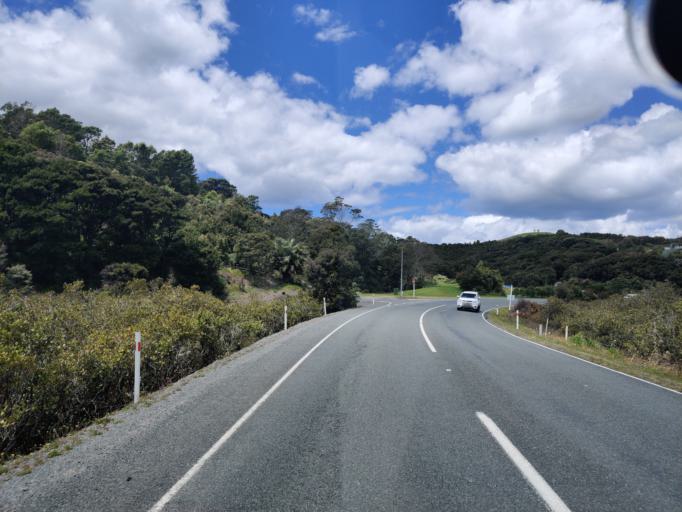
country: NZ
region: Northland
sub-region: Far North District
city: Paihia
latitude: -35.2735
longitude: 174.1392
